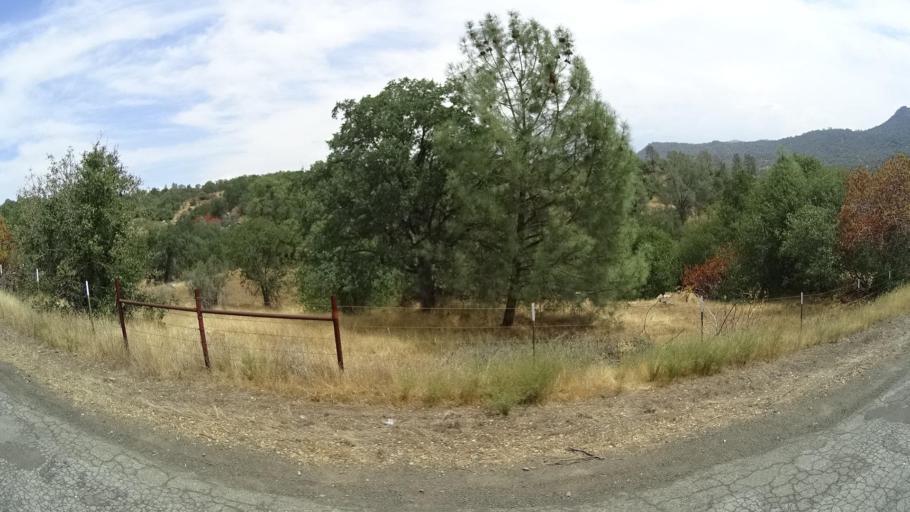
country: US
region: California
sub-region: Madera County
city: Ahwahnee
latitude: 37.3987
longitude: -119.8467
